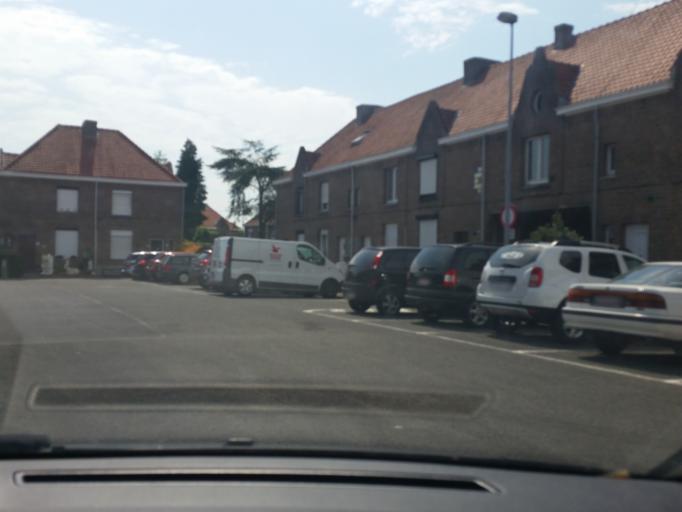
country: BE
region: Flanders
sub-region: Provincie Antwerpen
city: Mechelen
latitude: 51.0041
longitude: 4.4844
